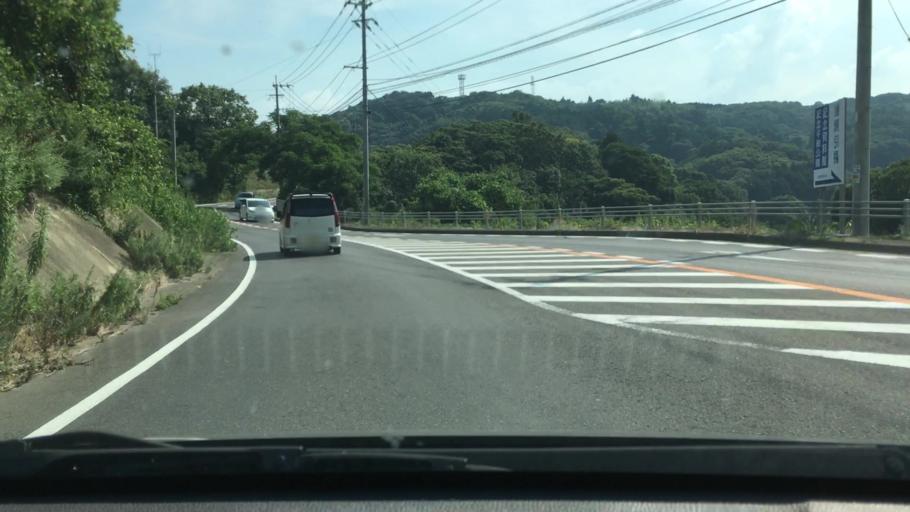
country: JP
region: Nagasaki
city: Sasebo
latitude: 33.0993
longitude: 129.7618
